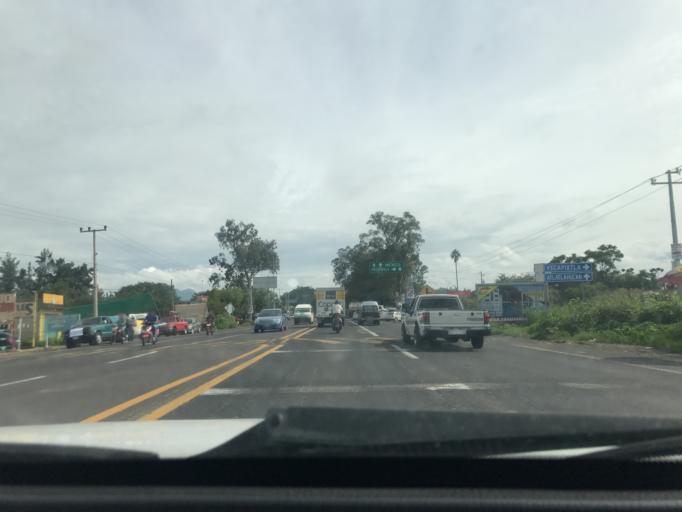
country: MX
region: Morelos
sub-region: Atlatlahucan
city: Colonia San Francisco
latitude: 18.8966
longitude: -98.9091
